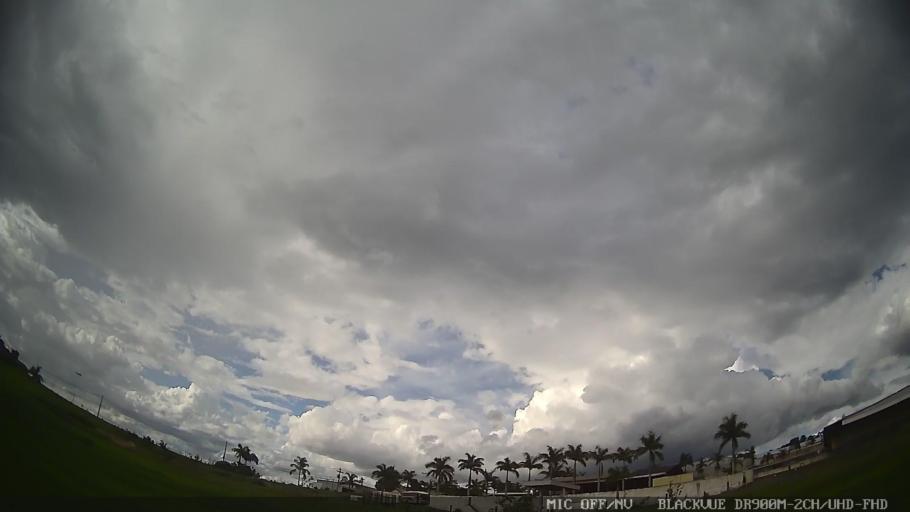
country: BR
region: Sao Paulo
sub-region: Jaguariuna
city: Jaguariuna
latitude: -22.6919
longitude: -47.0021
